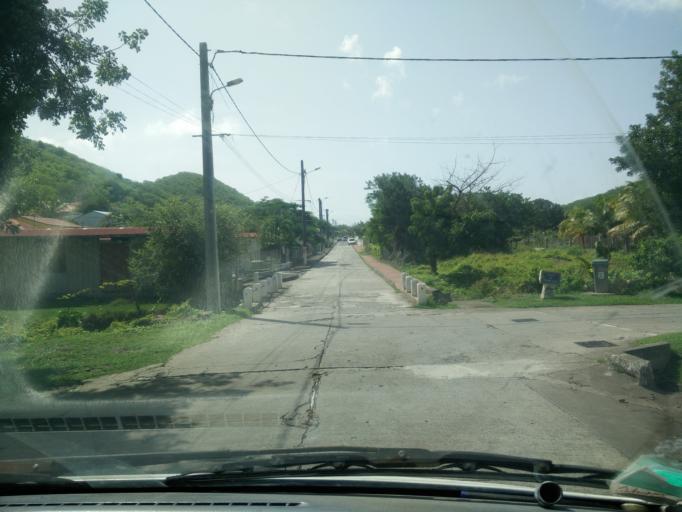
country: GP
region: Guadeloupe
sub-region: Guadeloupe
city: Terre-de-Bas
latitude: 15.8459
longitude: -61.6406
